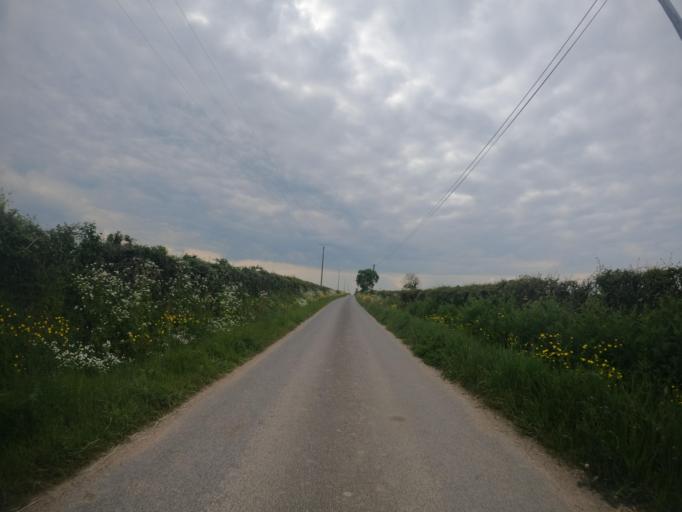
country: FR
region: Poitou-Charentes
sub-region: Departement des Deux-Sevres
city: Chiche
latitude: 46.8513
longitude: -0.3160
